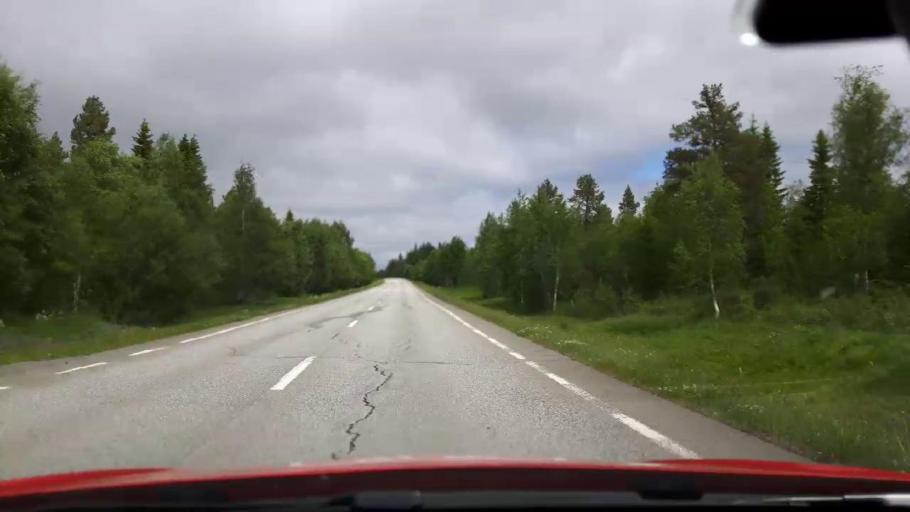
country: SE
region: Jaemtland
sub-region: Krokoms Kommun
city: Krokom
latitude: 63.4973
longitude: 14.5102
